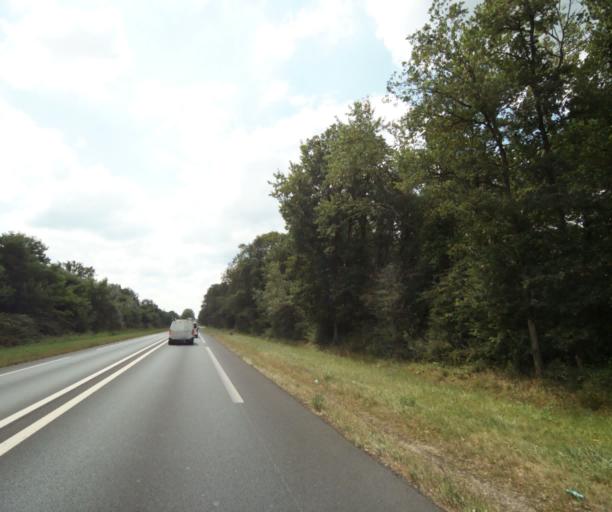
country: FR
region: Centre
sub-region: Departement du Loiret
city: Saint-Cyr-en-Val
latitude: 47.8229
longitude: 1.9234
